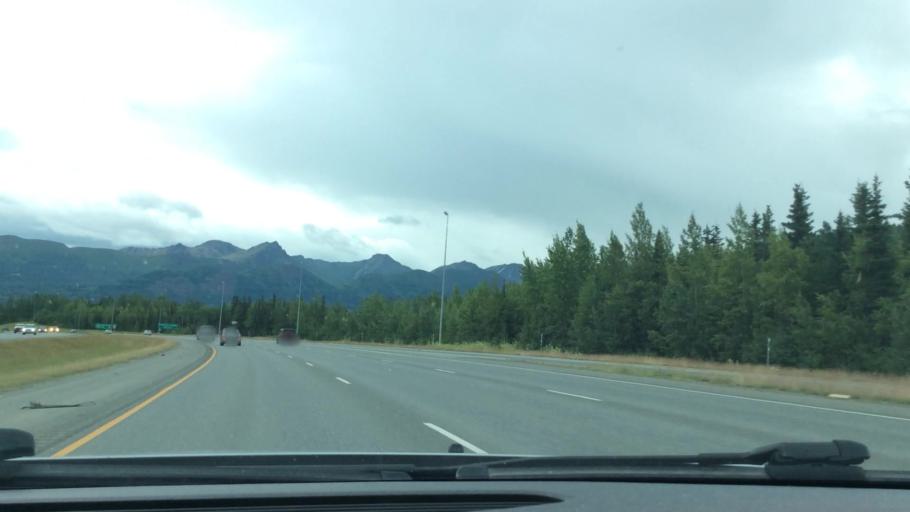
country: US
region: Alaska
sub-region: Anchorage Municipality
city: Eagle River
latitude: 61.2872
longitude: -149.5951
